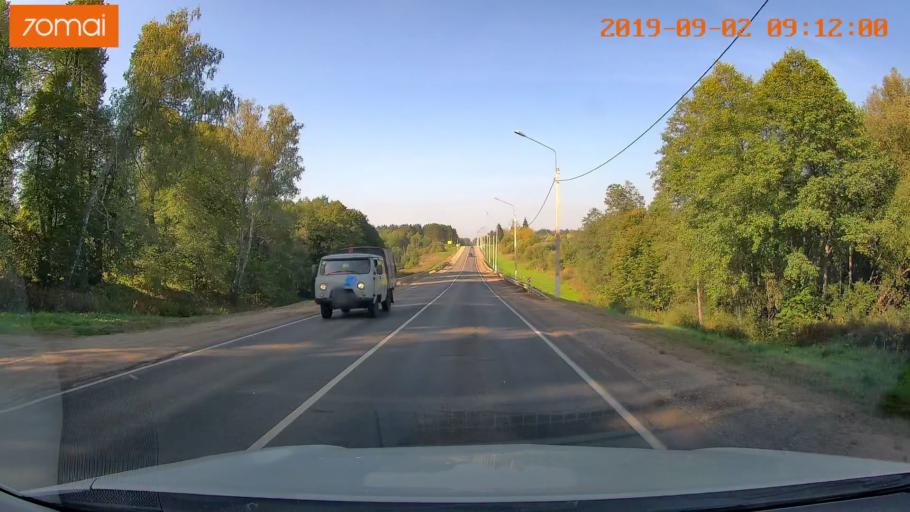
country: RU
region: Kaluga
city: Myatlevo
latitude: 54.8631
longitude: 35.5640
